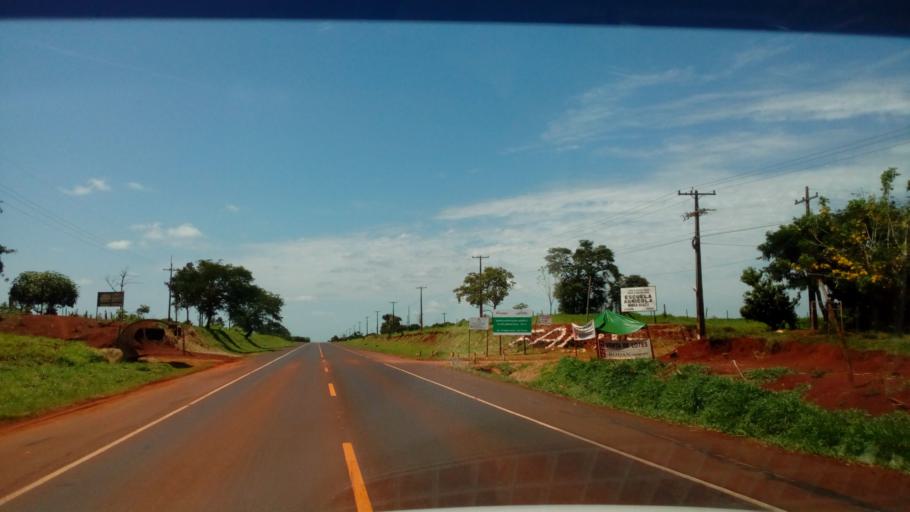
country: PY
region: Alto Parana
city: Colonia Yguazu
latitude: -25.5199
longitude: -54.8999
